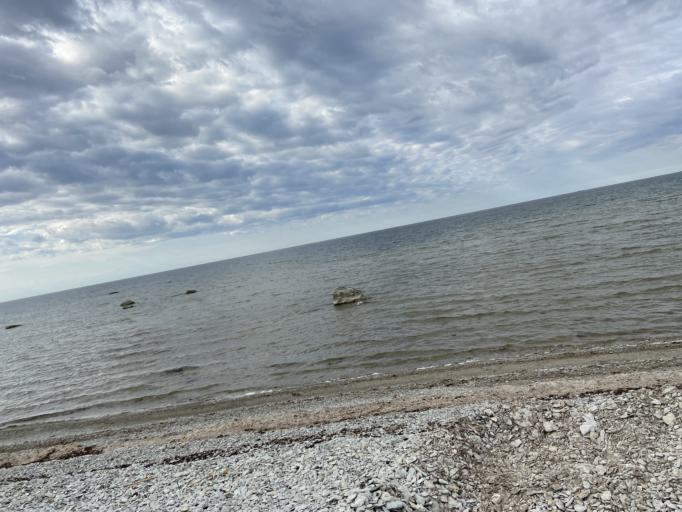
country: EE
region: Harju
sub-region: Paldiski linn
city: Paldiski
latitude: 59.2700
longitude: 23.7625
